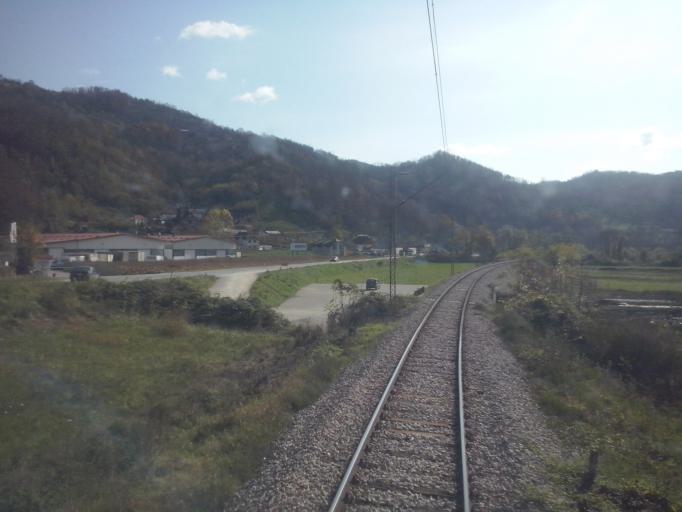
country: RS
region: Central Serbia
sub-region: Zlatiborski Okrug
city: Pozega
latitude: 43.9108
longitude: 20.0001
